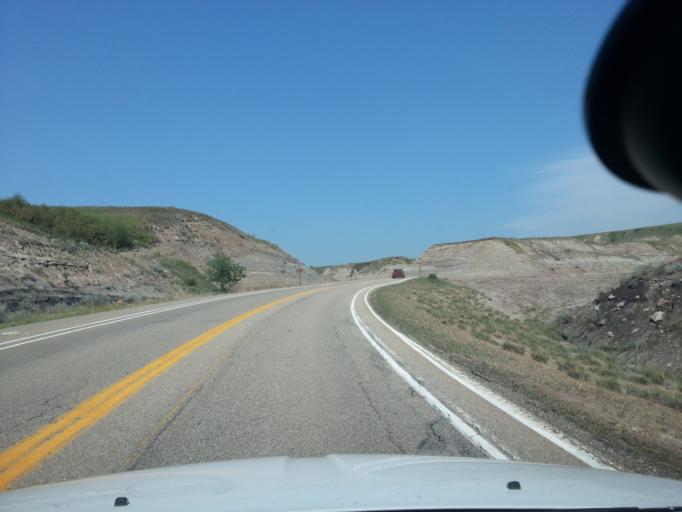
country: CA
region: Alberta
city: Three Hills
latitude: 51.4769
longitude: -112.7855
